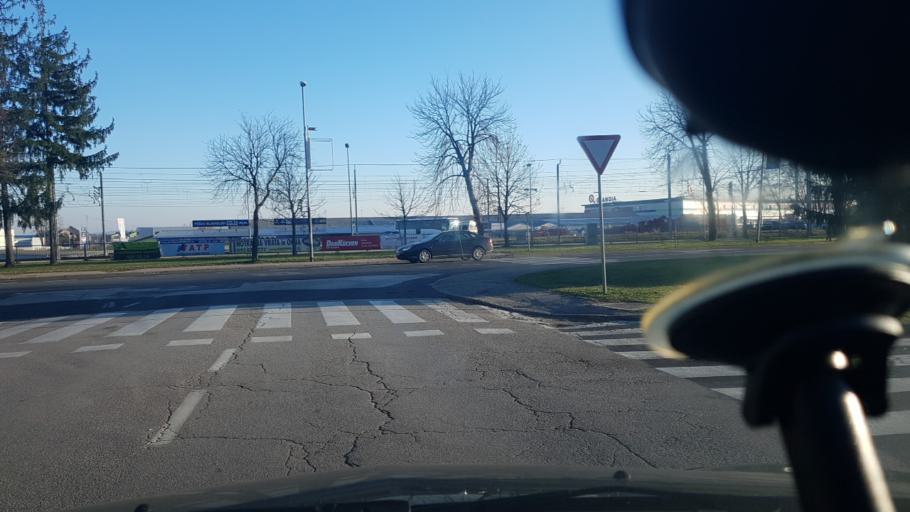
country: SI
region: Ptuj
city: Ptuj
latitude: 46.4218
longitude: 15.8772
